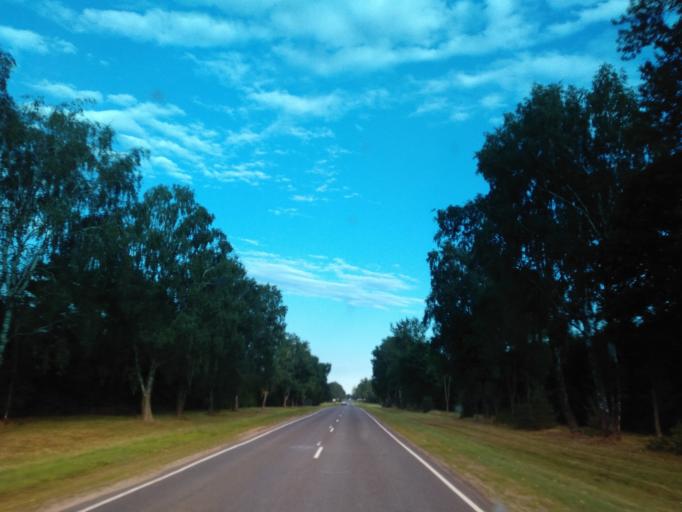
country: BY
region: Minsk
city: Uzda
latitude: 53.4344
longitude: 27.3386
